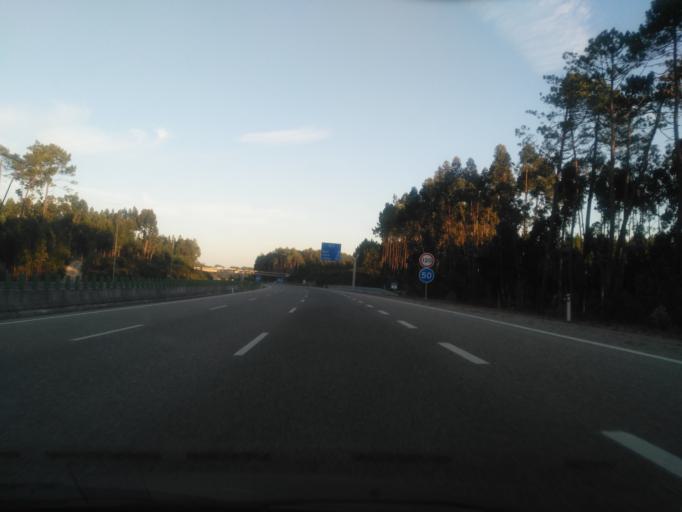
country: PT
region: Leiria
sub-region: Pombal
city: Lourical
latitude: 39.9883
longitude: -8.7946
